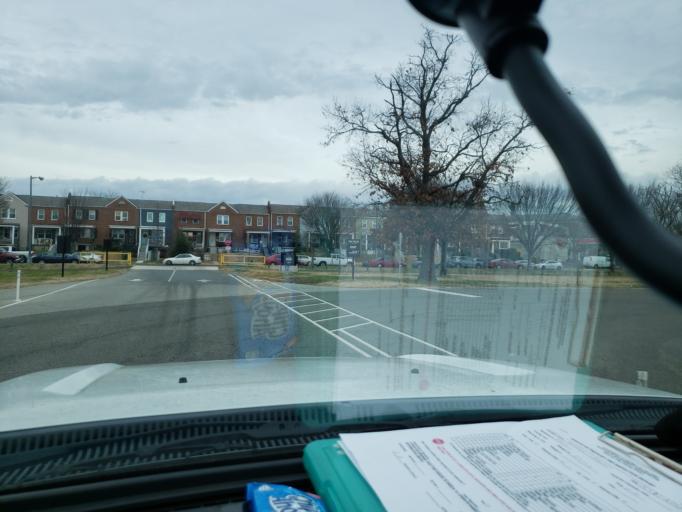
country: US
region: Maryland
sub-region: Prince George's County
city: Colmar Manor
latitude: 38.8964
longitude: -76.9697
